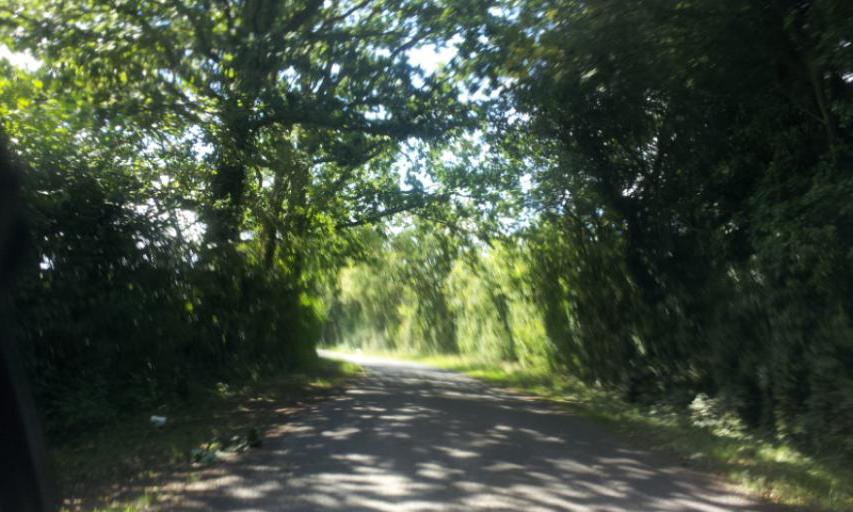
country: GB
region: England
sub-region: Kent
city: Marden
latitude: 51.2014
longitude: 0.5119
